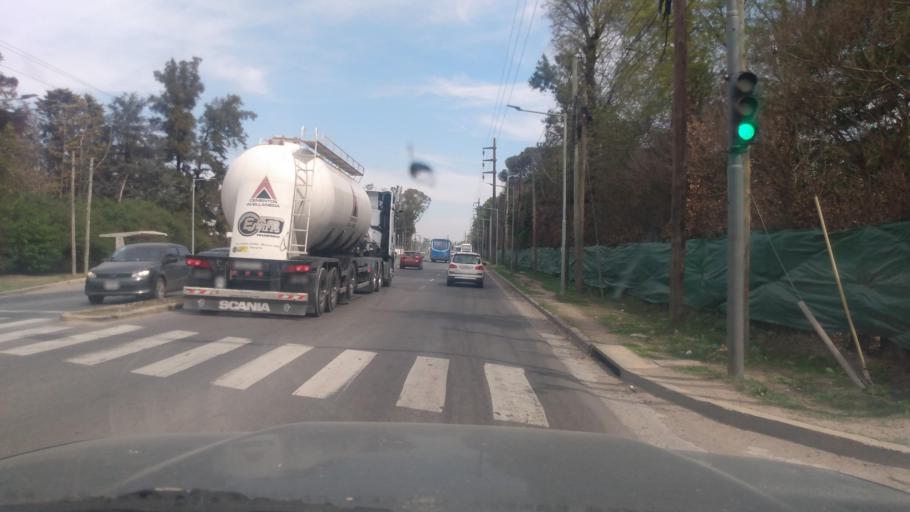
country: AR
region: Buenos Aires
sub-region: Partido de Pilar
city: Pilar
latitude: -34.4397
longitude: -58.8961
